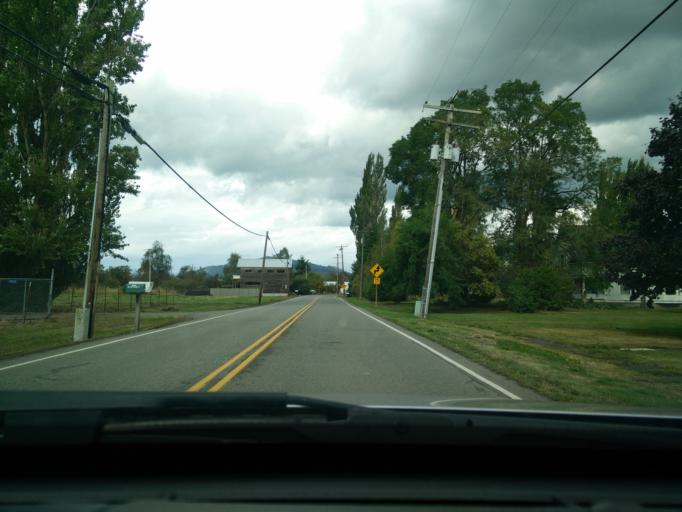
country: US
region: Washington
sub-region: Skagit County
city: Burlington
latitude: 48.5597
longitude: -122.4443
